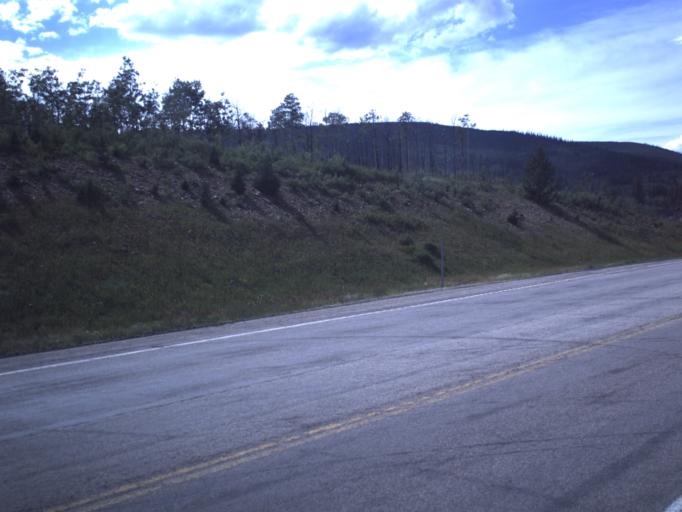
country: US
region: Utah
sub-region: Wasatch County
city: Heber
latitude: 40.2986
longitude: -111.2528
